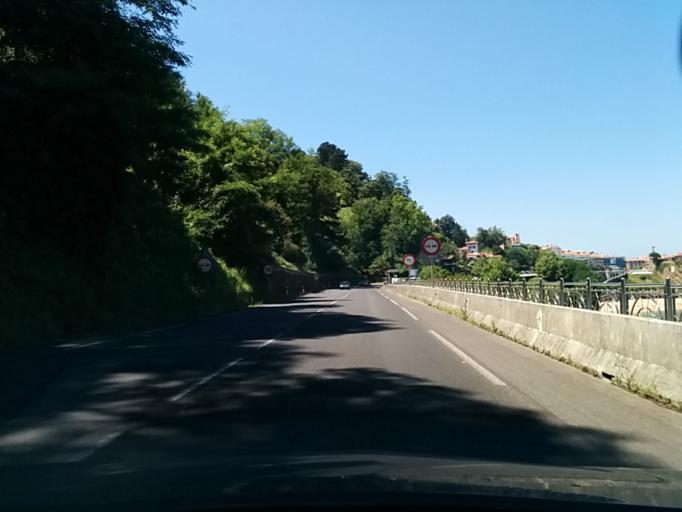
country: ES
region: Basque Country
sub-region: Provincia de Guipuzcoa
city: Getaria
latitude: 43.2987
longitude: -2.1979
